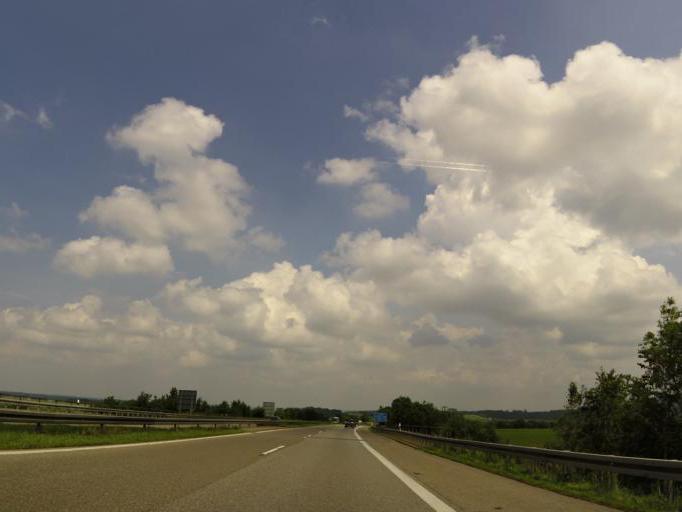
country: DE
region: Baden-Wuerttemberg
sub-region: Regierungsbezirk Stuttgart
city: Westhausen
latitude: 48.8926
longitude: 10.1675
